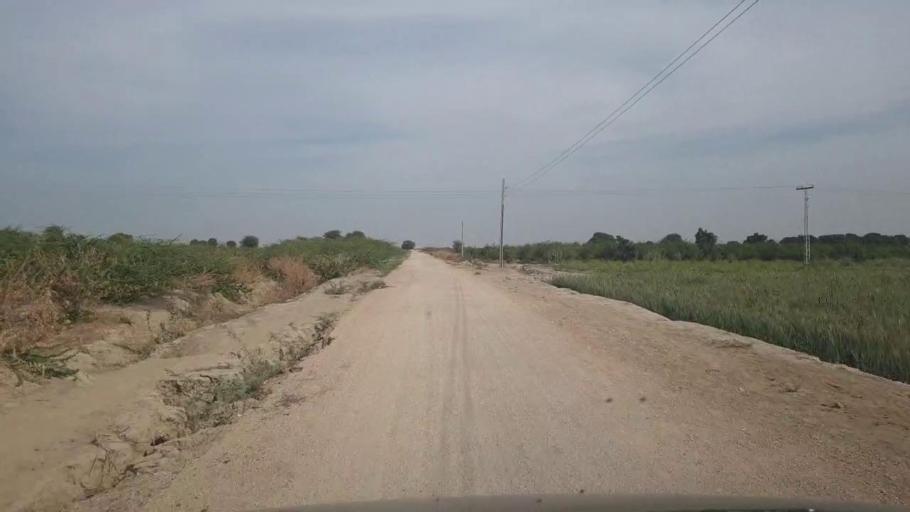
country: PK
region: Sindh
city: Kunri
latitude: 25.2296
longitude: 69.5921
